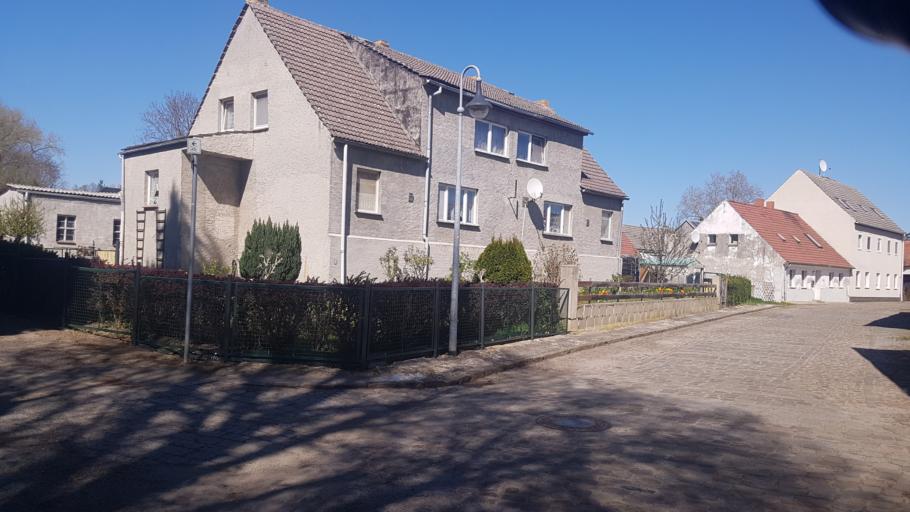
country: DE
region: Brandenburg
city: Sonnewalde
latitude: 51.6958
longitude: 13.6451
